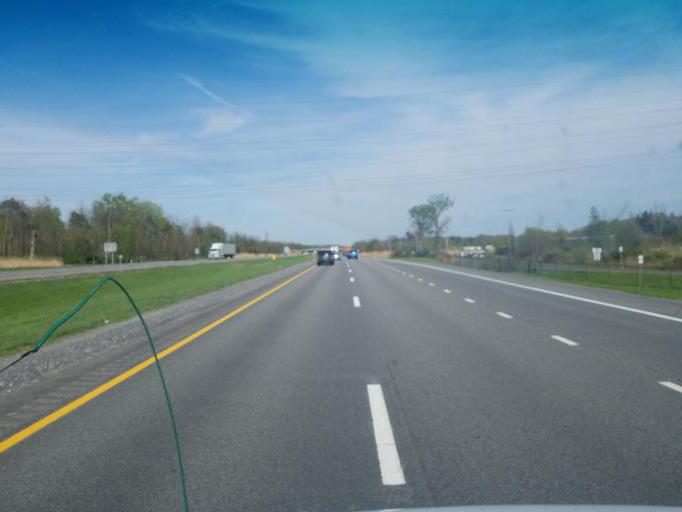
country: US
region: New York
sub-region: Onondaga County
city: Minoa
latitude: 43.0947
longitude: -76.0416
